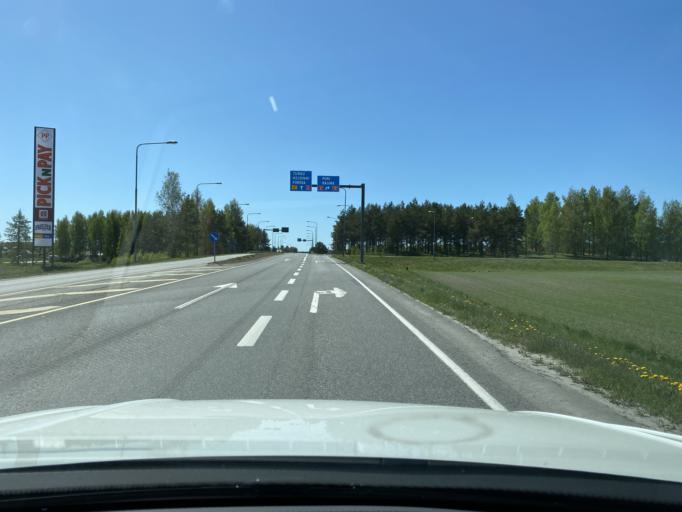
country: FI
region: Satakunta
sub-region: Pori
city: Huittinen
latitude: 61.1714
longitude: 22.6771
